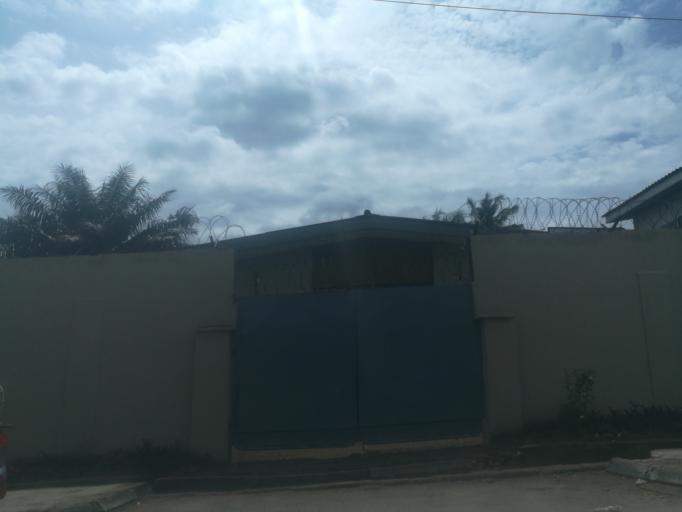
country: NG
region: Lagos
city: Somolu
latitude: 6.5575
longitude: 3.3648
